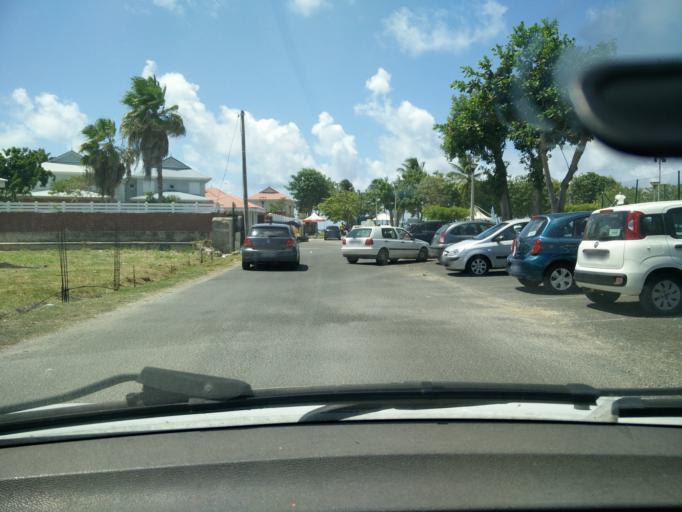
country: GP
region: Guadeloupe
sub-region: Guadeloupe
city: Le Moule
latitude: 16.3320
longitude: -61.3393
